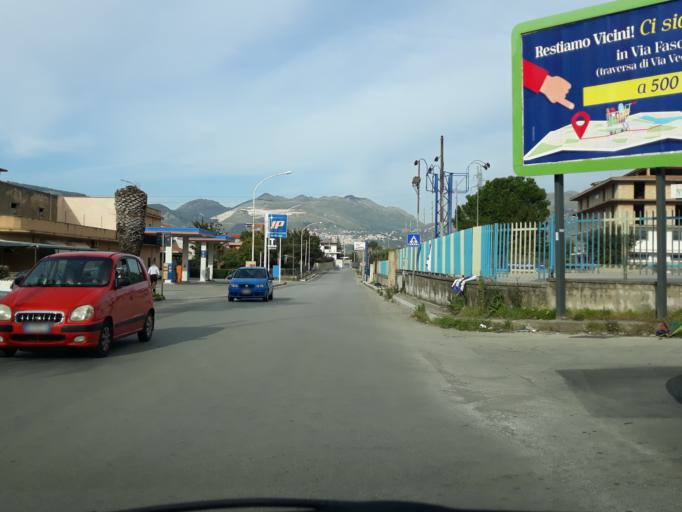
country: IT
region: Sicily
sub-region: Palermo
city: Partinico
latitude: 38.0555
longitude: 13.1297
